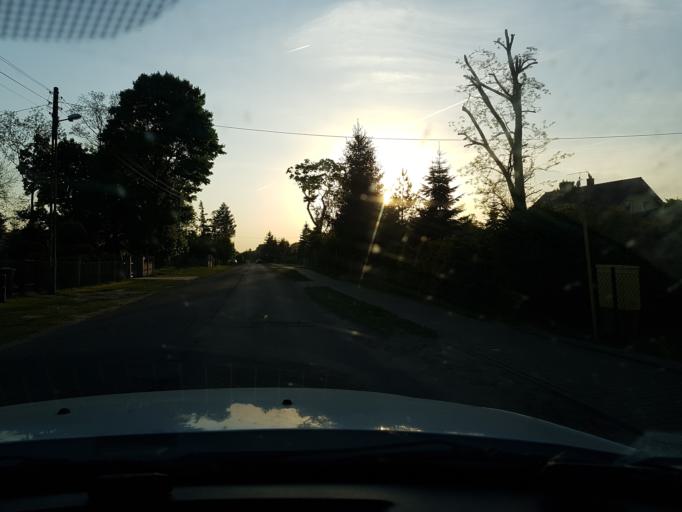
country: PL
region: West Pomeranian Voivodeship
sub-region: Powiat stargardzki
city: Kobylanka
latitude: 53.3656
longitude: 14.8652
